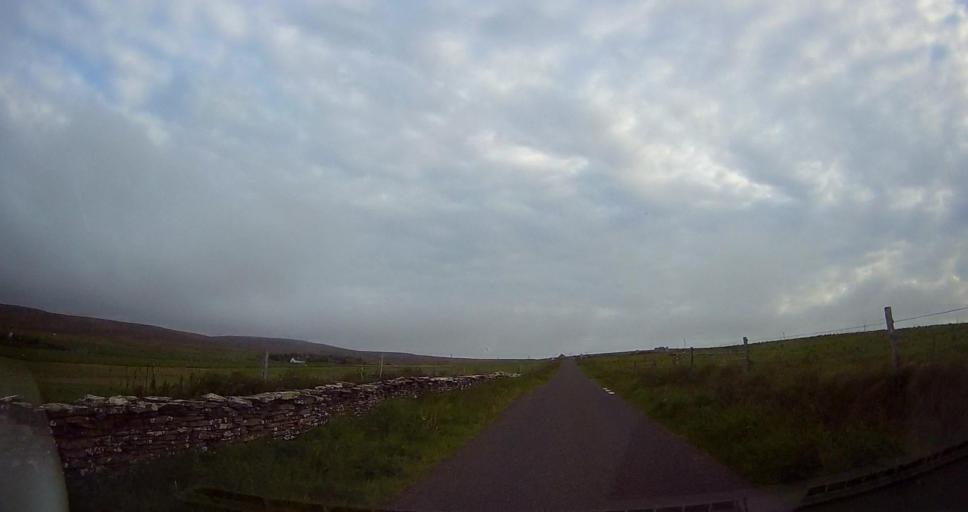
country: GB
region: Scotland
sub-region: Orkney Islands
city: Orkney
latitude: 59.1131
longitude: -3.1136
